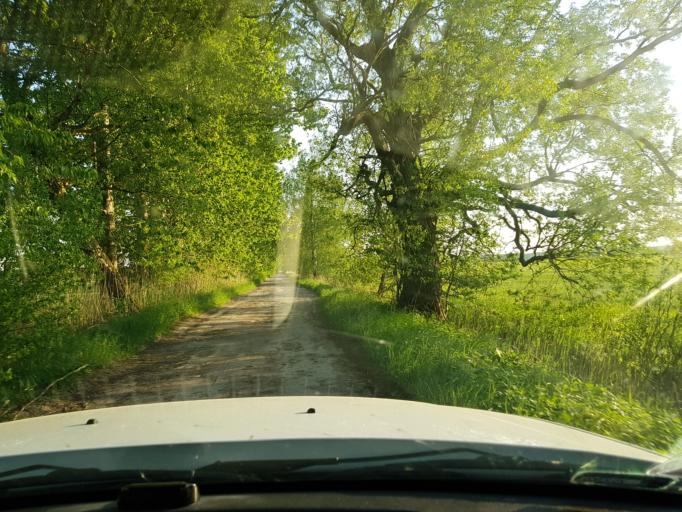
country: PL
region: West Pomeranian Voivodeship
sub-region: Powiat stargardzki
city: Kobylanka
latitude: 53.4078
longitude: 14.8943
